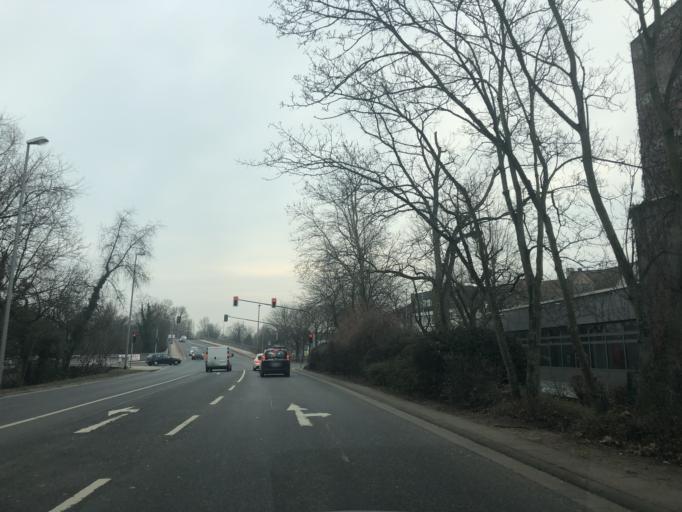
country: DE
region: Hesse
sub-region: Regierungsbezirk Darmstadt
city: Hattersheim
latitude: 50.0702
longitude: 8.4881
